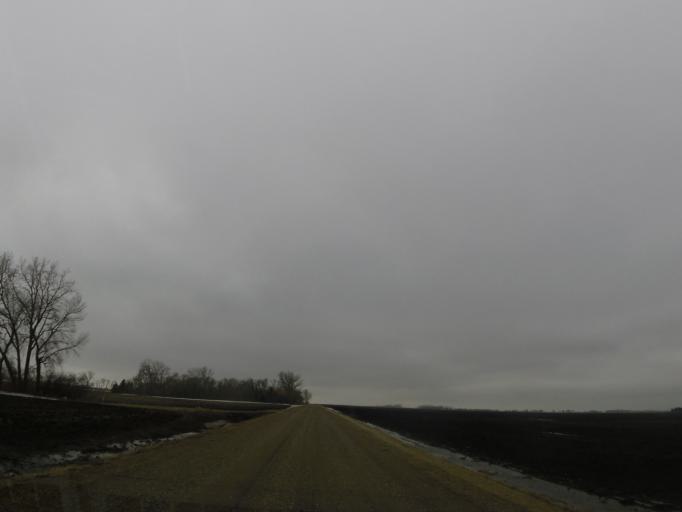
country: US
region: North Dakota
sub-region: Walsh County
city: Grafton
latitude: 48.3946
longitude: -97.2119
